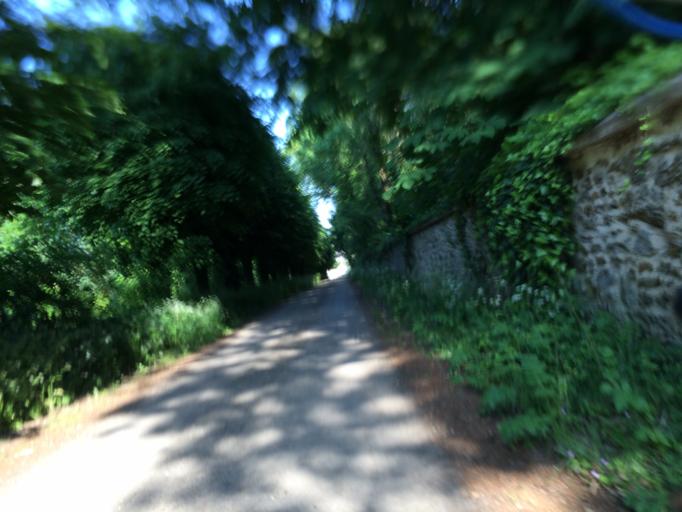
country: FR
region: Ile-de-France
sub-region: Departement de l'Essonne
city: Fleury-Merogis
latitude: 48.6312
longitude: 2.3589
